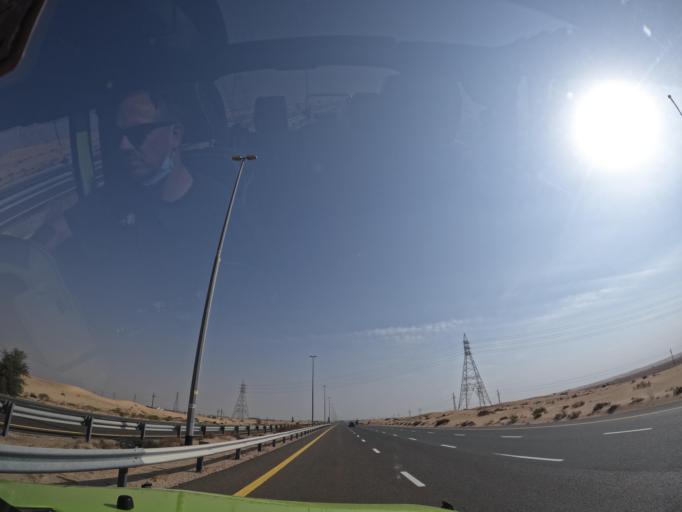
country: AE
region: Ash Shariqah
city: Sharjah
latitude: 25.0216
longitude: 55.5530
